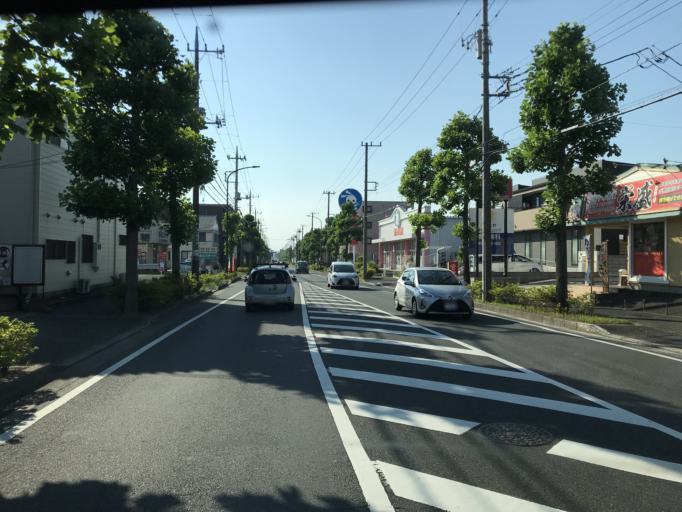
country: JP
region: Chiba
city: Chiba
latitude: 35.5424
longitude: 140.1853
